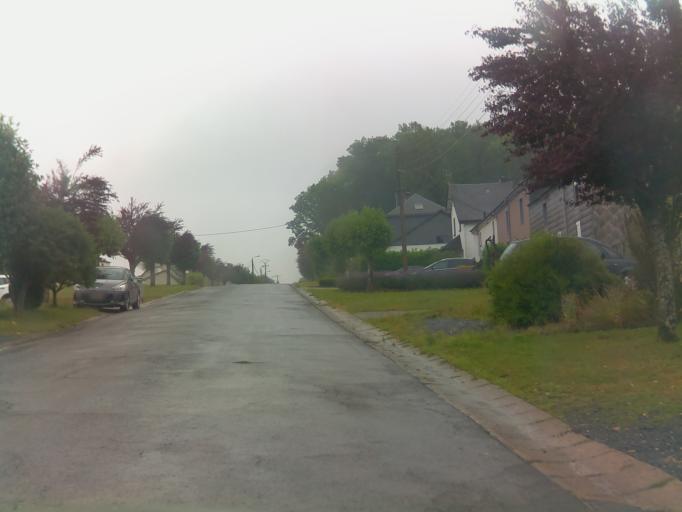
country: BE
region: Wallonia
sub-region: Province du Luxembourg
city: Habay-la-Vieille
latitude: 49.7258
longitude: 5.6170
